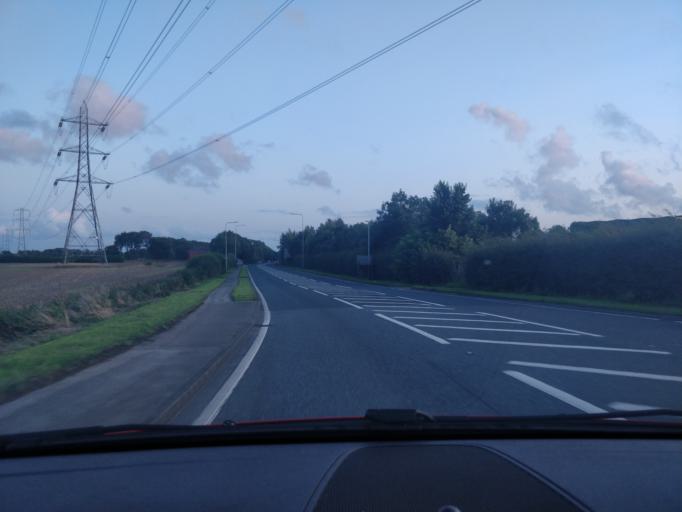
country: GB
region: England
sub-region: Lancashire
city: Tarleton
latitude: 53.6859
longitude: -2.8161
